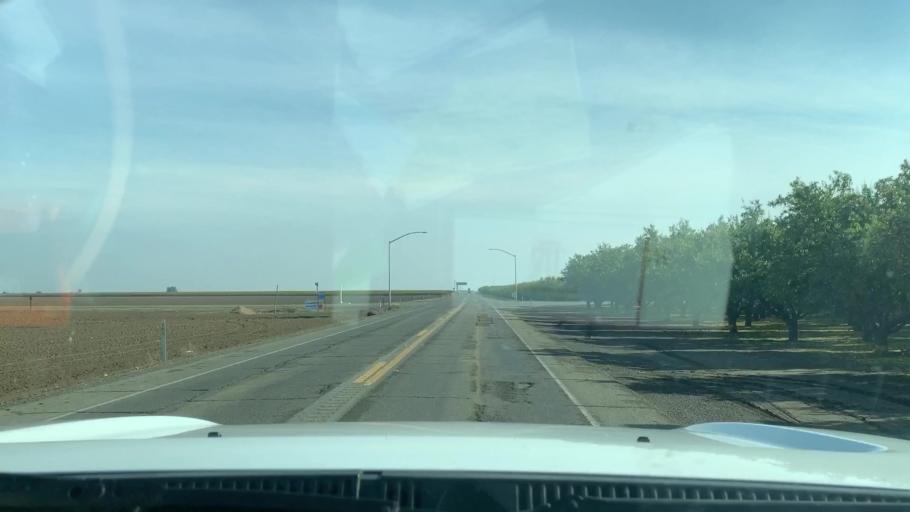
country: US
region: California
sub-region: Fresno County
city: Huron
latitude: 36.2548
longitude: -120.2124
